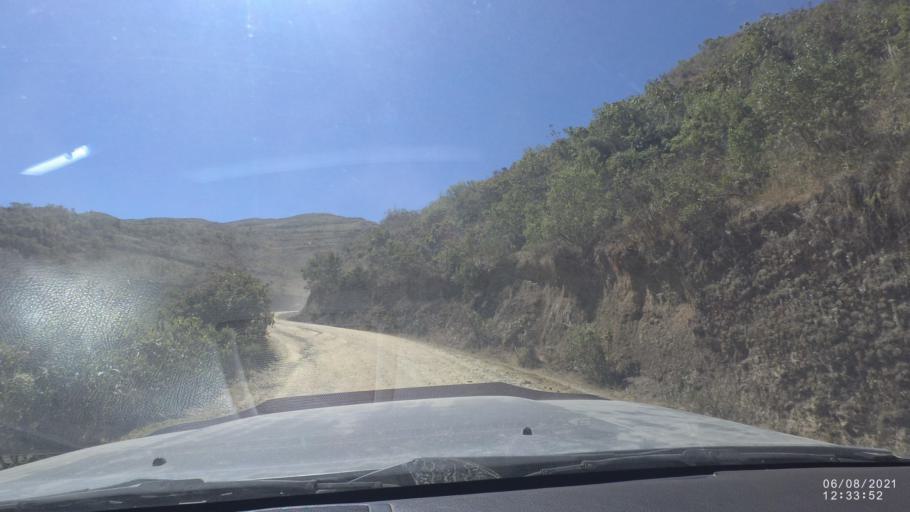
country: BO
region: Cochabamba
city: Colchani
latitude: -16.7785
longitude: -66.6442
